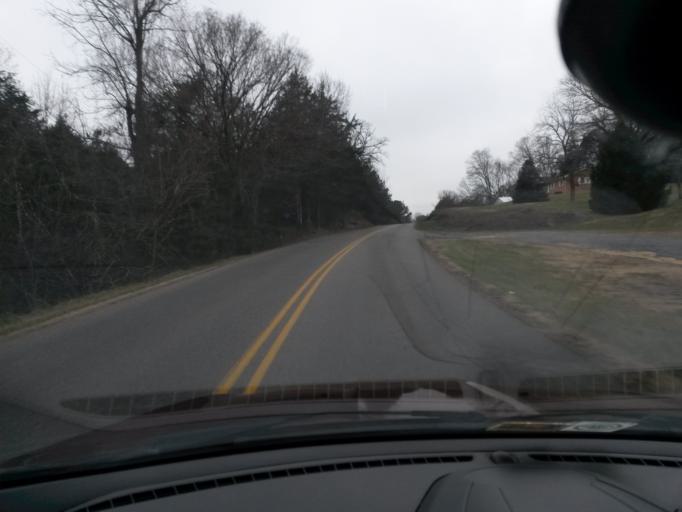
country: US
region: Virginia
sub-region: City of Buena Vista
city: Buena Vista
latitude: 37.7871
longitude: -79.3647
